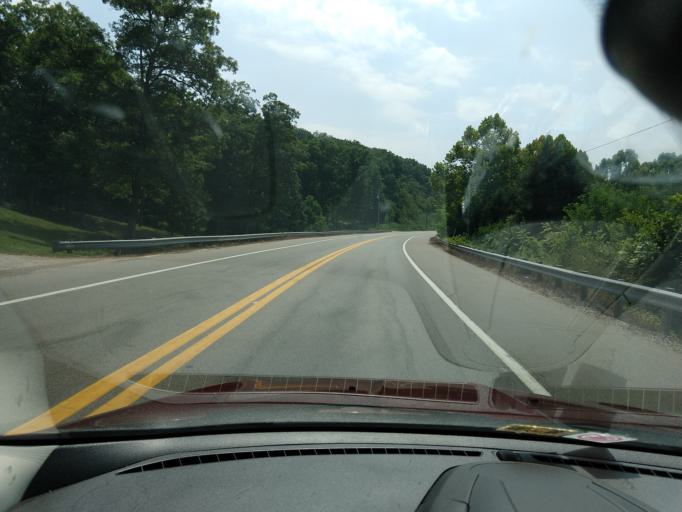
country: US
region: West Virginia
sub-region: Jackson County
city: Ravenswood
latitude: 38.8601
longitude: -81.8069
